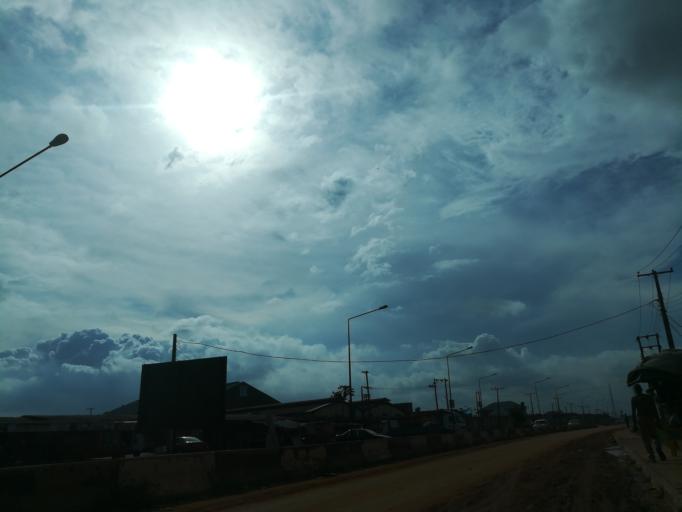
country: NG
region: Lagos
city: Ebute Ikorodu
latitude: 6.5932
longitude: 3.5069
